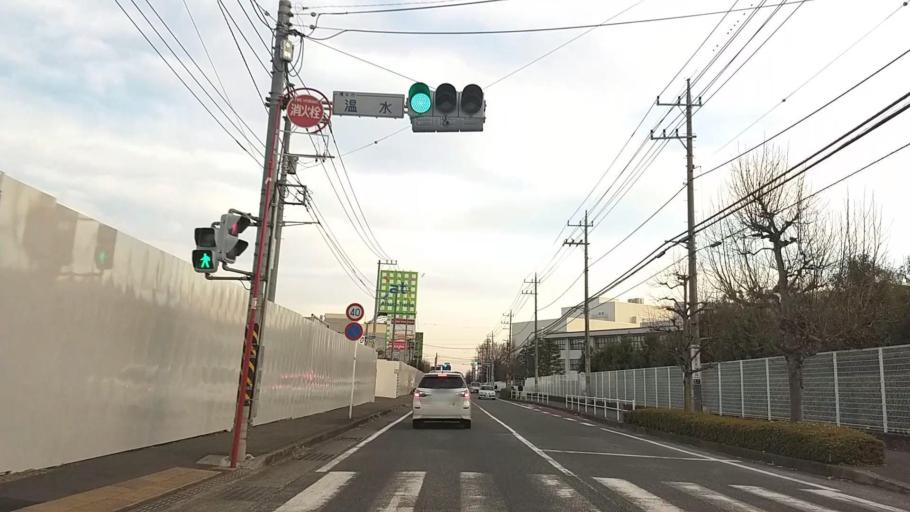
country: JP
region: Kanagawa
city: Atsugi
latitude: 35.4487
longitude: 139.3400
